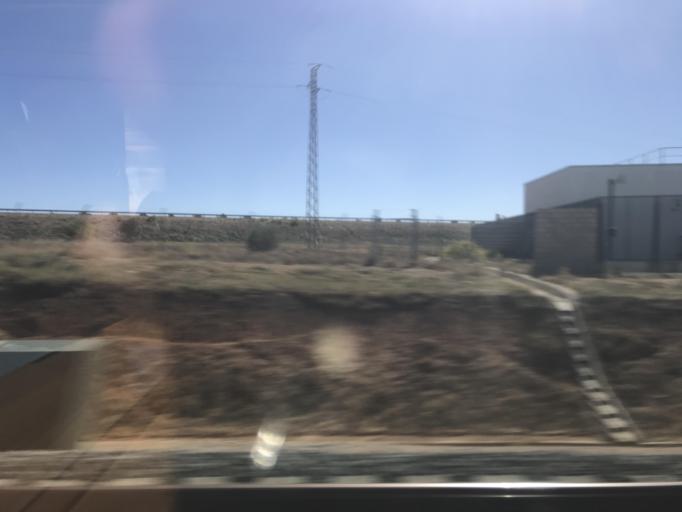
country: ES
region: Castille-La Mancha
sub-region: Province of Toledo
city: Santa Cruz de la Zarza
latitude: 39.9522
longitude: -3.2443
